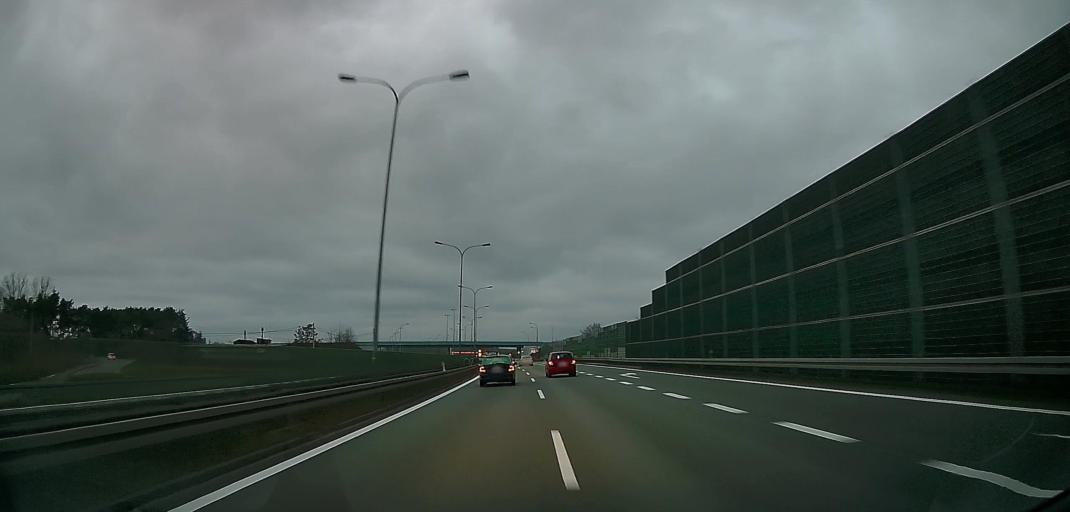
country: PL
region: Masovian Voivodeship
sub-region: Powiat bialobrzeski
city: Stara Blotnica
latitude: 51.5672
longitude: 21.0245
